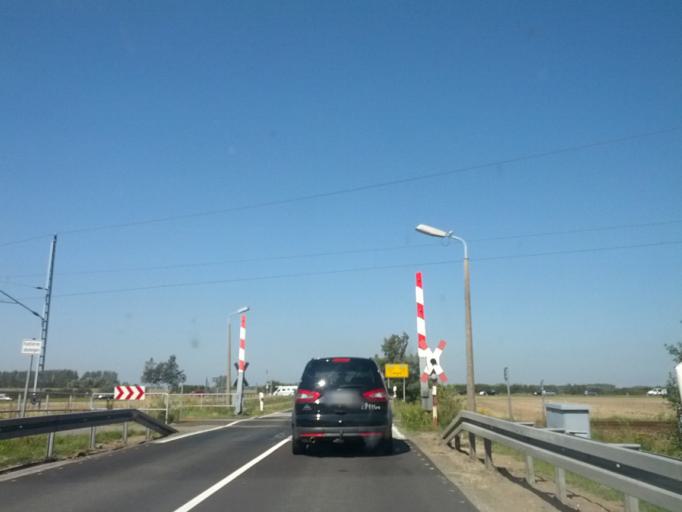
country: DE
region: Mecklenburg-Vorpommern
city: Sagard
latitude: 54.5087
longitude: 13.5377
